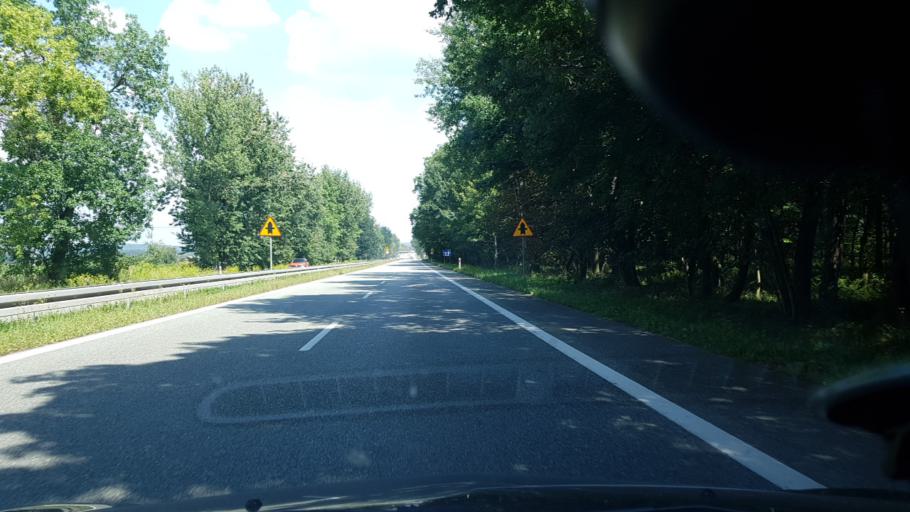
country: PL
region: Silesian Voivodeship
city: Gardawice
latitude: 50.0971
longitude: 18.7722
